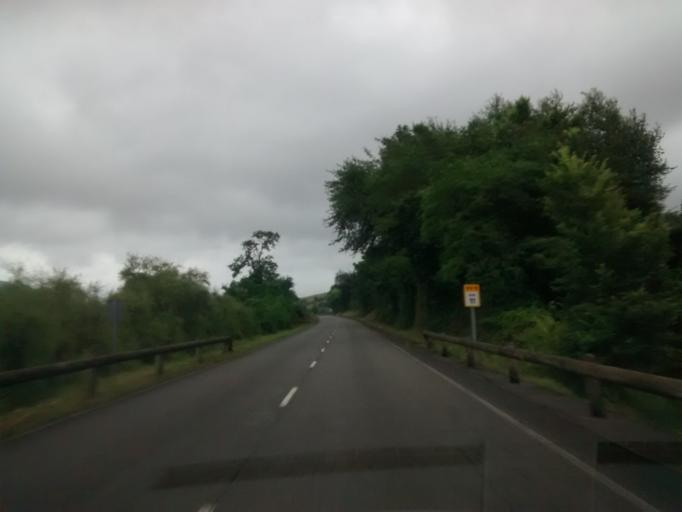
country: ES
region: Asturias
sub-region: Province of Asturias
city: Villaviciosa
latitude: 43.5054
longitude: -5.4237
